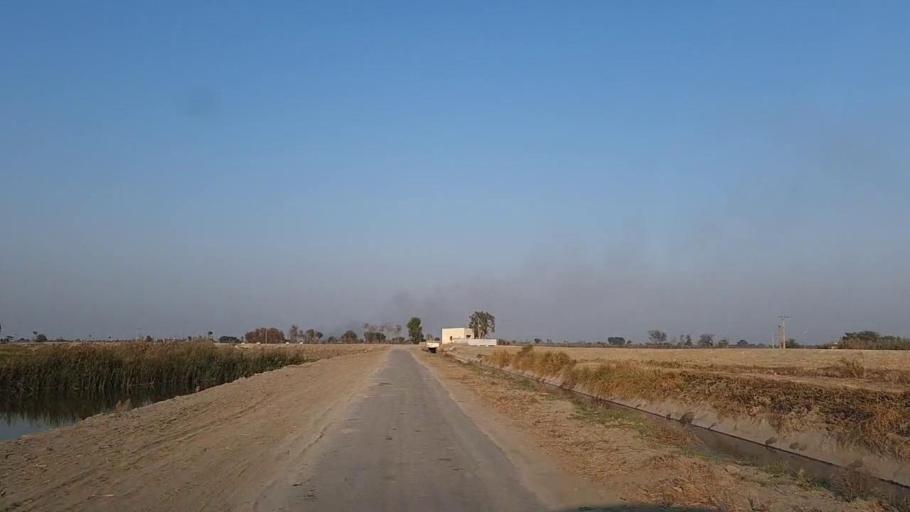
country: PK
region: Sindh
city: Daur
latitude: 26.5101
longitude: 68.2925
